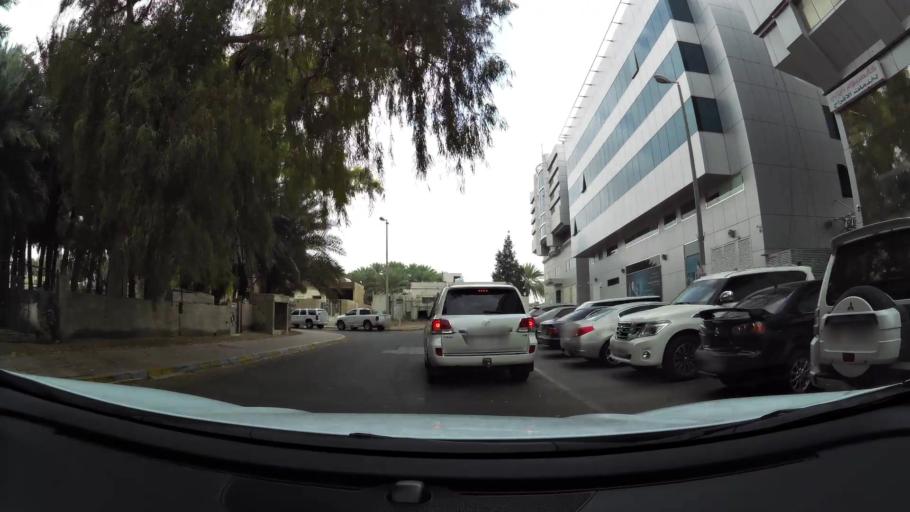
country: AE
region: Abu Dhabi
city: Al Ain
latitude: 24.2285
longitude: 55.7615
